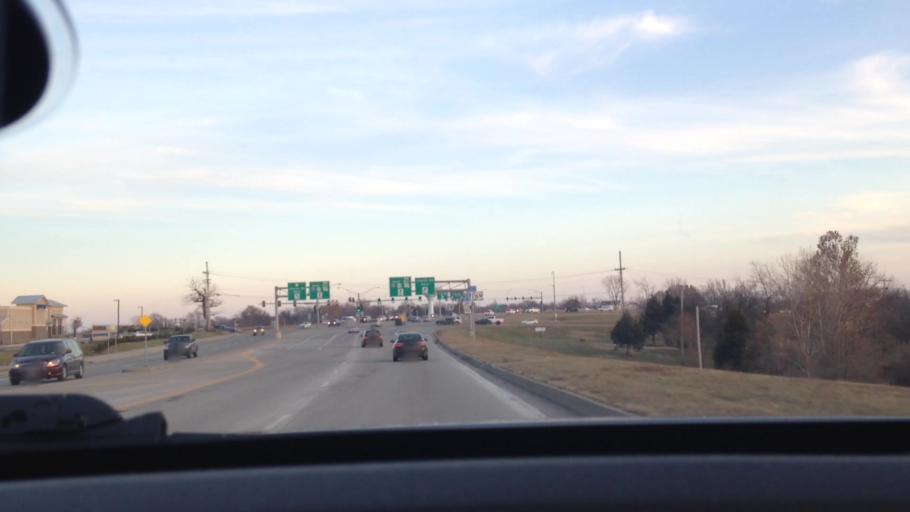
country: US
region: Missouri
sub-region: Clay County
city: Liberty
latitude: 39.2670
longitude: -94.4504
